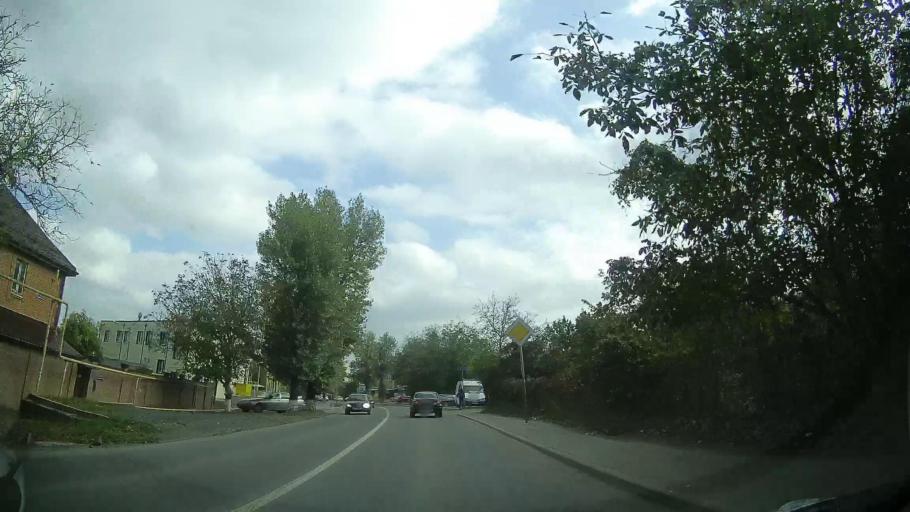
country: RU
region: Rostov
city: Severnyy
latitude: 47.2849
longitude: 39.6681
